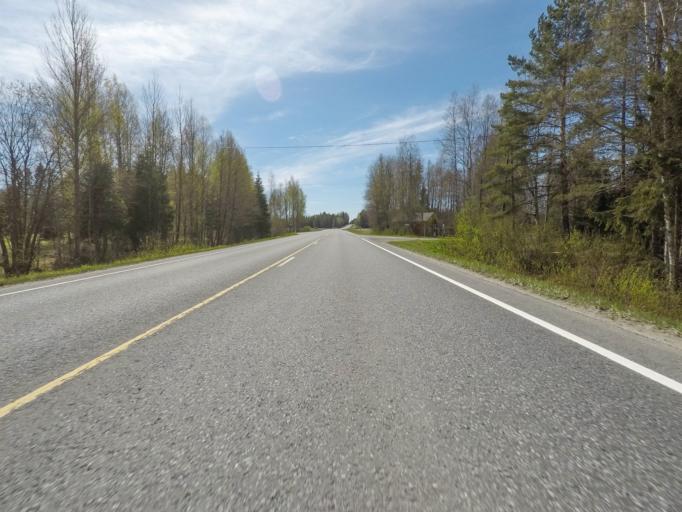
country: FI
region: Pirkanmaa
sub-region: Etelae-Pirkanmaa
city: Urjala
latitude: 61.0138
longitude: 23.4771
